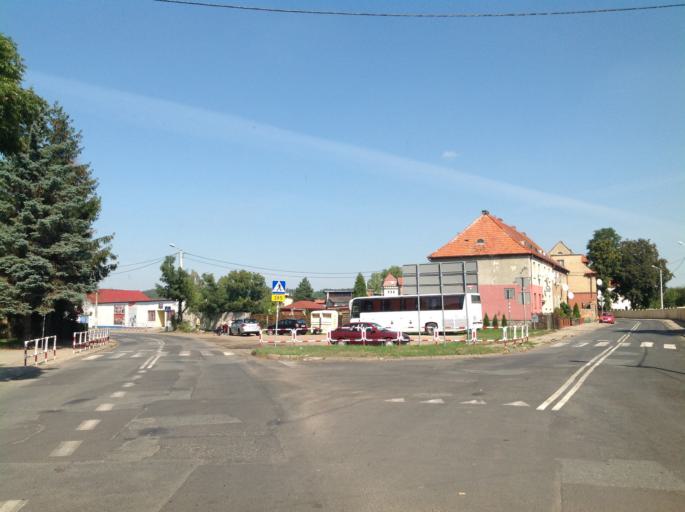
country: PL
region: Lower Silesian Voivodeship
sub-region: Powiat zabkowicki
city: Ziebice
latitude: 50.6055
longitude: 17.0497
